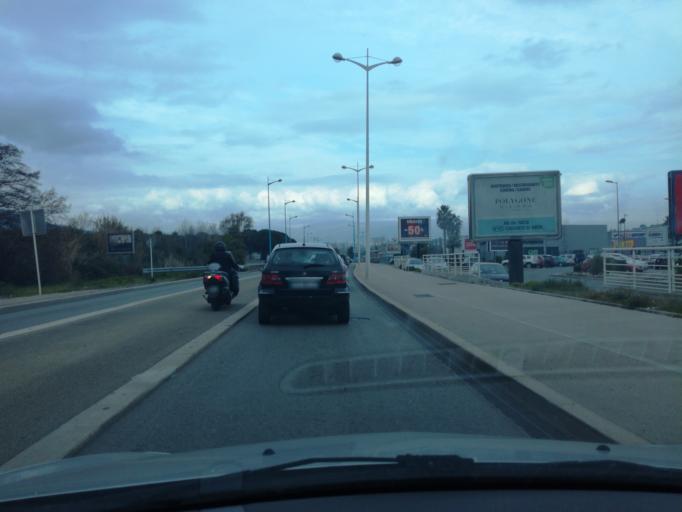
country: FR
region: Provence-Alpes-Cote d'Azur
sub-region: Departement des Alpes-Maritimes
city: Mandelieu-la-Napoule
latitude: 43.5522
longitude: 6.9554
